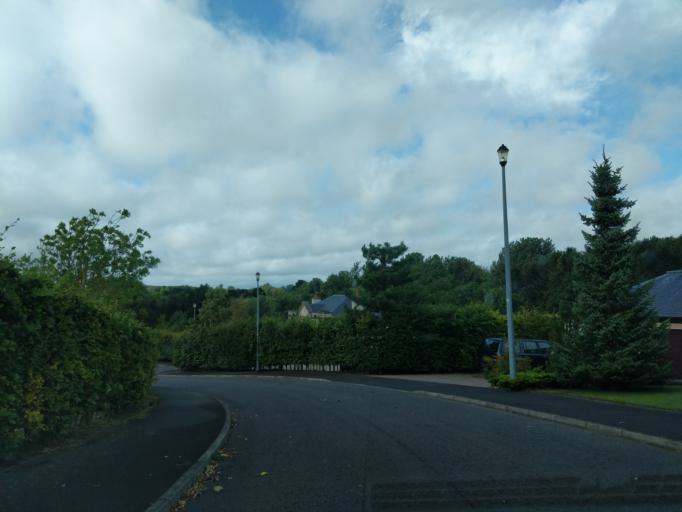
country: GB
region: Scotland
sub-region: The Scottish Borders
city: Kelso
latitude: 55.5658
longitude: -2.4705
